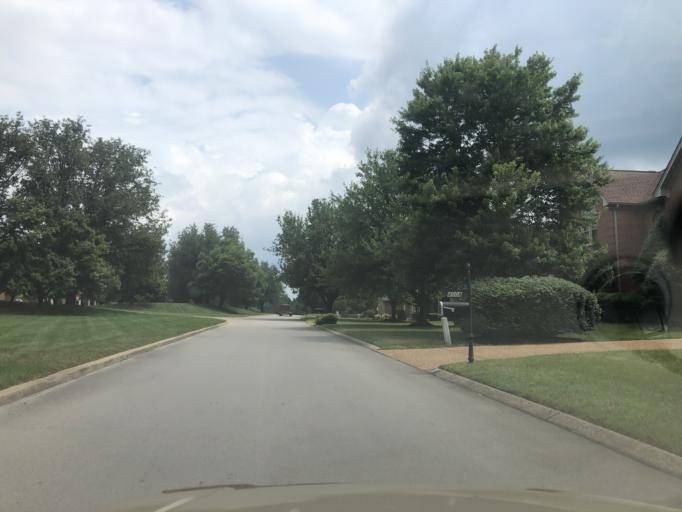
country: US
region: Tennessee
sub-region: Davidson County
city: Lakewood
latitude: 36.2315
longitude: -86.6074
